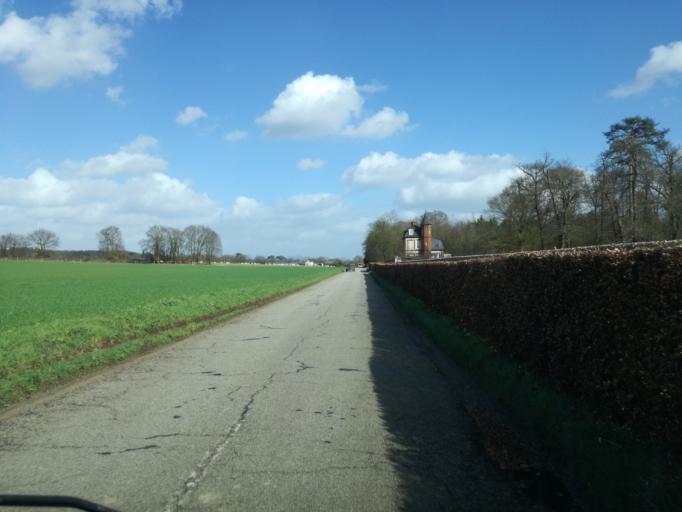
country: FR
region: Haute-Normandie
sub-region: Departement de la Seine-Maritime
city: Sahurs
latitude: 49.3580
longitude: 0.9641
